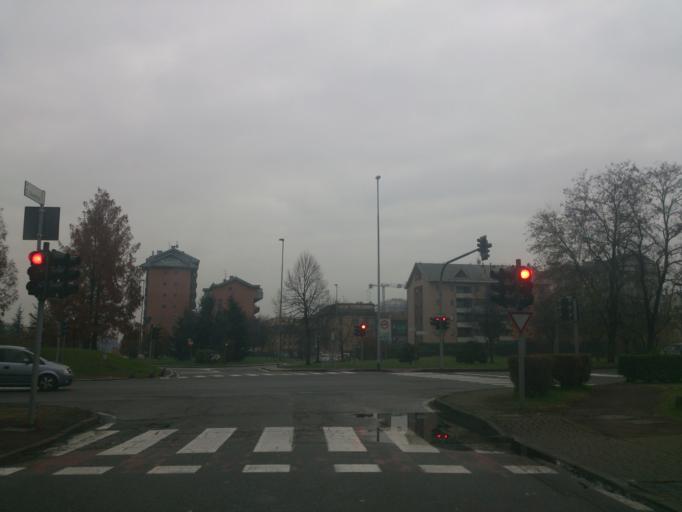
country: IT
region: Lombardy
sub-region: Citta metropolitana di Milano
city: San Donato Milanese
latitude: 45.4117
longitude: 9.2656
